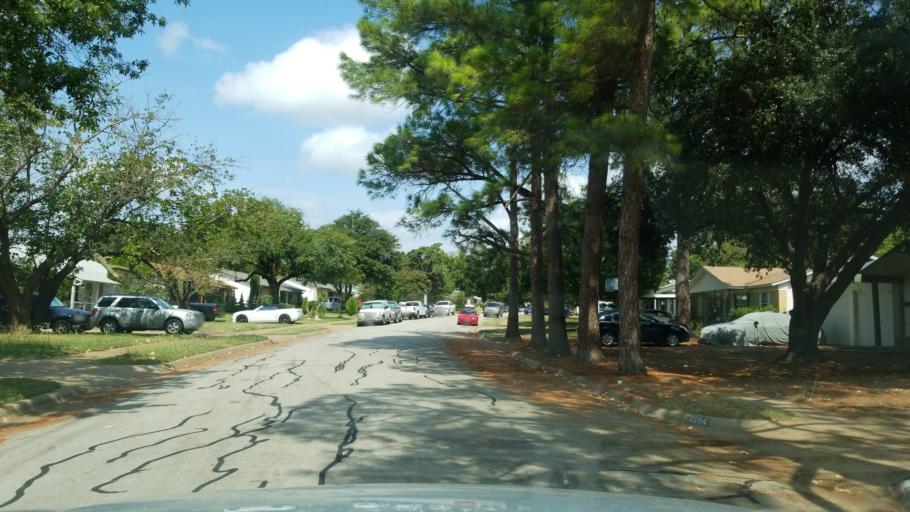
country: US
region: Texas
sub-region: Tarrant County
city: Euless
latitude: 32.8499
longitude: -97.0934
